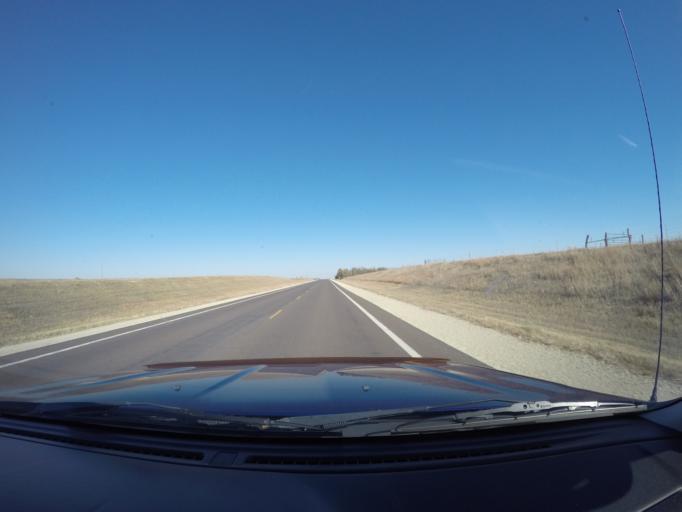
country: US
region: Kansas
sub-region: Marshall County
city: Blue Rapids
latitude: 39.6545
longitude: -96.7505
